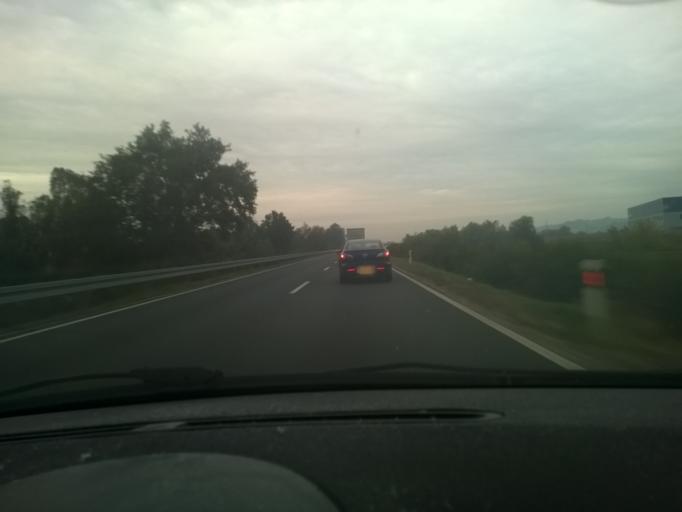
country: HR
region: Zagrebacka
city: Jakovlje
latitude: 45.9519
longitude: 15.8267
